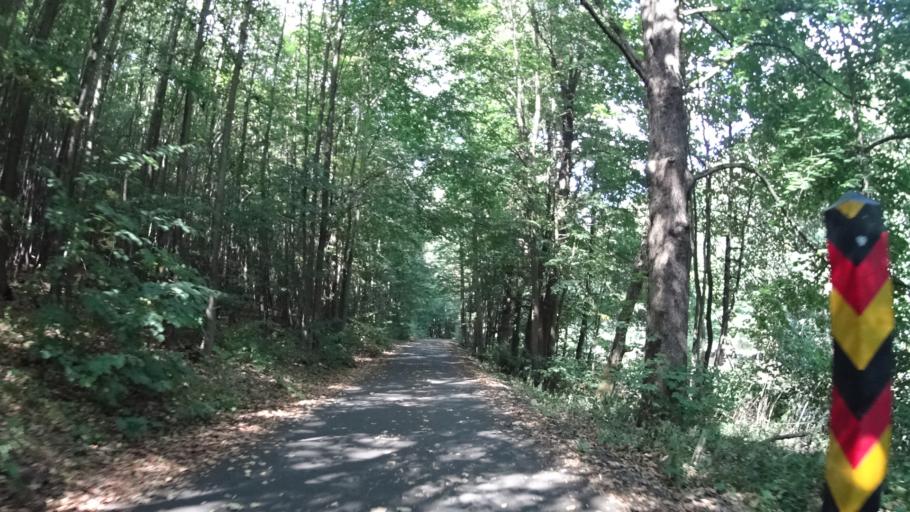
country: DE
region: Saxony
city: Hirschfelde
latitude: 50.9659
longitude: 14.9027
